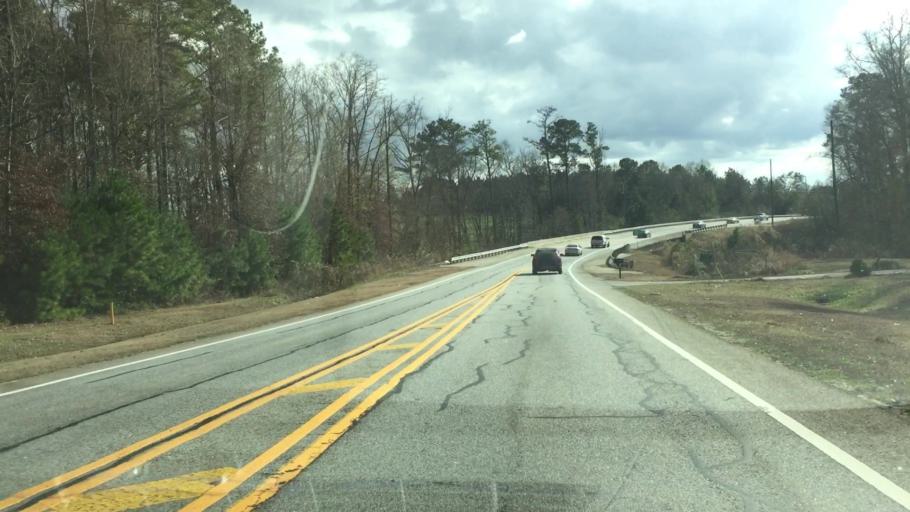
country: US
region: Georgia
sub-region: Henry County
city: McDonough
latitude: 33.4772
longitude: -84.1396
